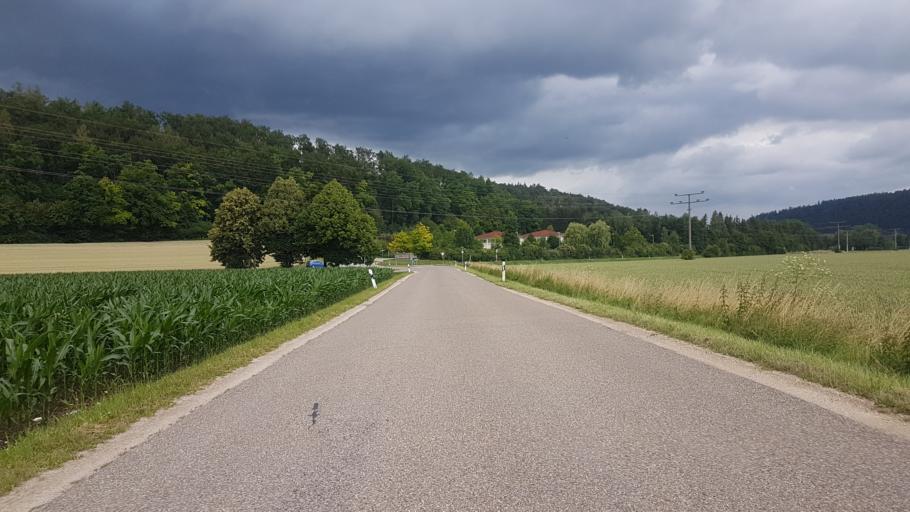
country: DE
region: Bavaria
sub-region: Upper Bavaria
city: Denkendorf
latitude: 48.9951
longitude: 11.4357
